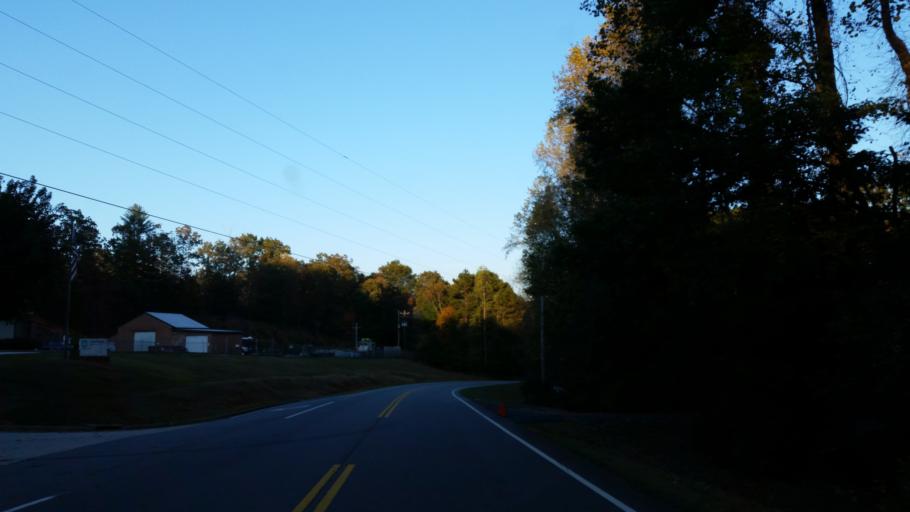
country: US
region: Georgia
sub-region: Lumpkin County
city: Dahlonega
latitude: 34.5278
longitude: -84.0259
